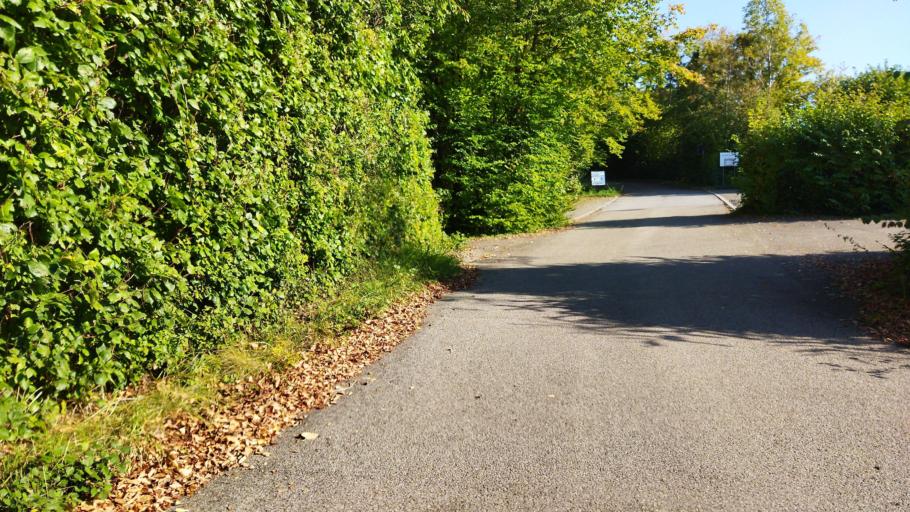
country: DE
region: Baden-Wuerttemberg
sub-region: Regierungsbezirk Stuttgart
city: Grossbottwar
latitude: 49.0292
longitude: 9.2735
